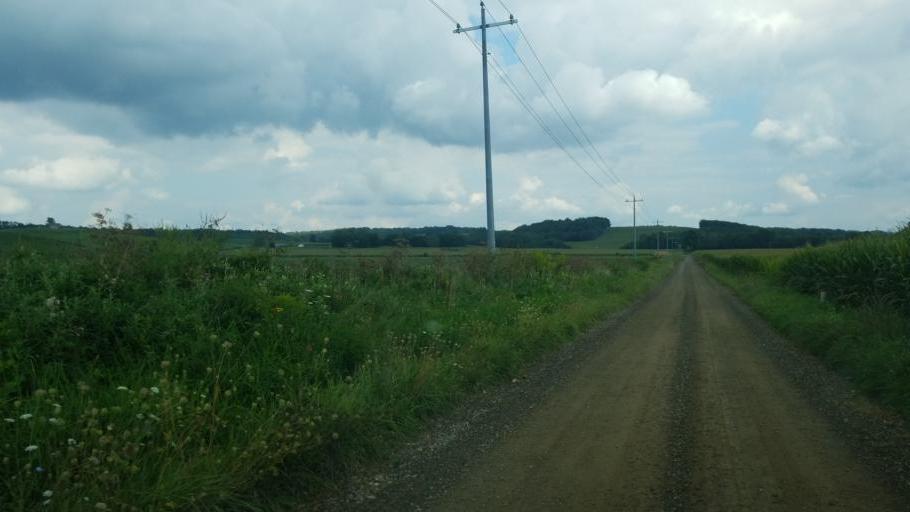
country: US
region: Ohio
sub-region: Knox County
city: Oak Hill
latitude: 40.4219
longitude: -82.2520
